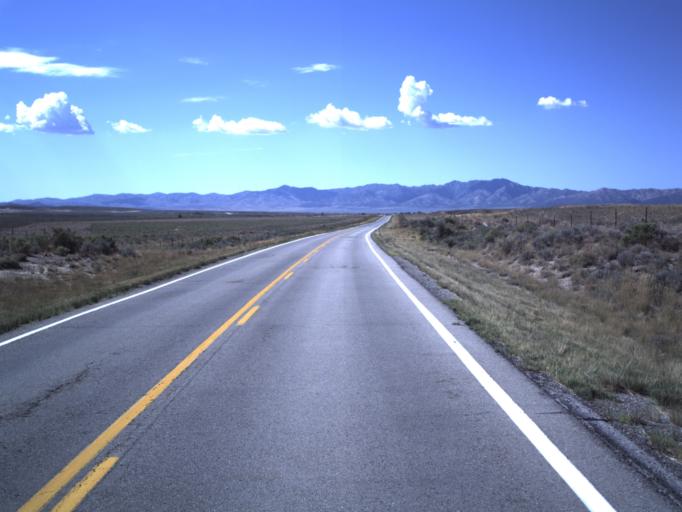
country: US
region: Utah
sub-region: Tooele County
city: Tooele
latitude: 40.2110
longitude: -112.4075
